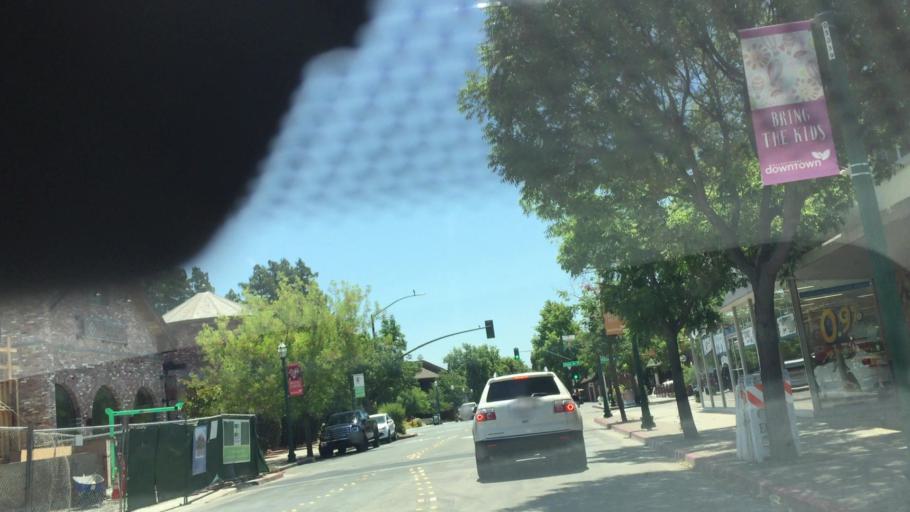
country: US
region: California
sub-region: Contra Costa County
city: Walnut Creek
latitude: 37.9025
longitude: -122.0624
